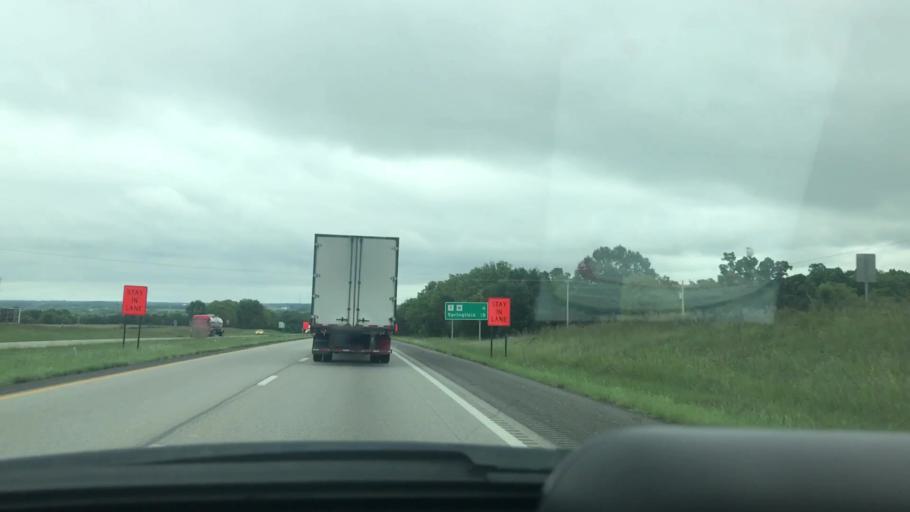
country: US
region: Missouri
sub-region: Greene County
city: Republic
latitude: 37.1857
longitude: -93.5525
